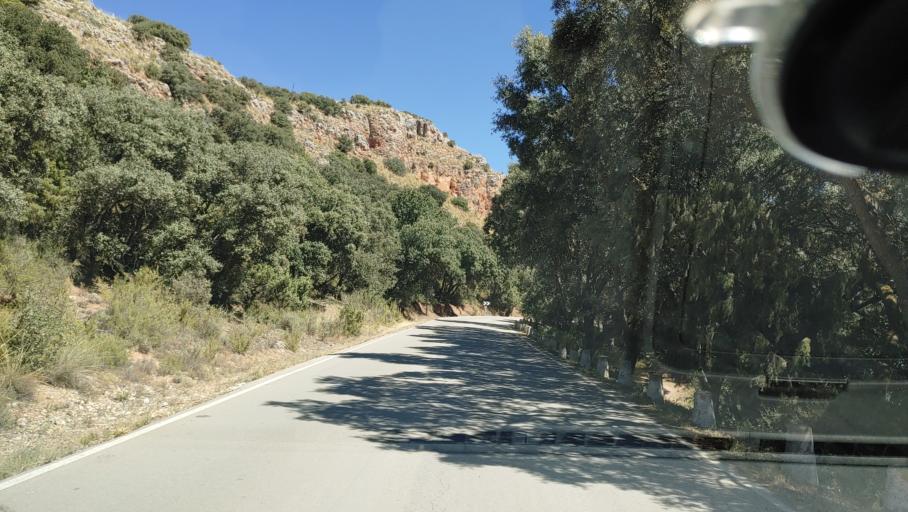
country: ES
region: Castille-La Mancha
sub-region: Provincia de Ciudad Real
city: Ruidera
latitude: 38.9519
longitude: -2.8595
